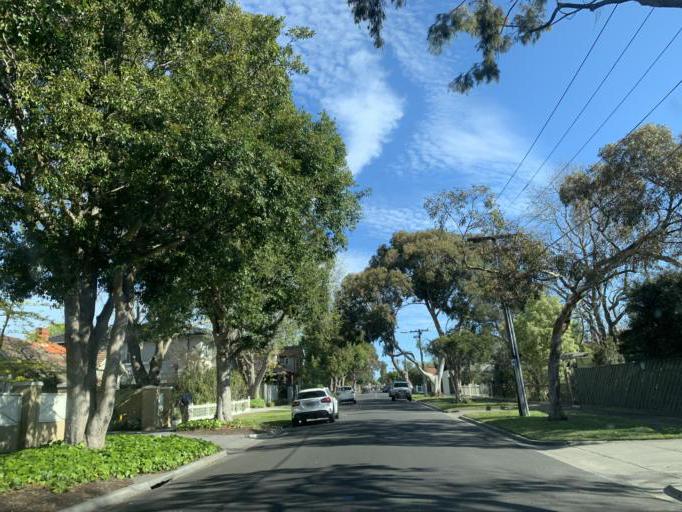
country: AU
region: Victoria
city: Hampton
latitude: -37.9506
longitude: 145.0150
